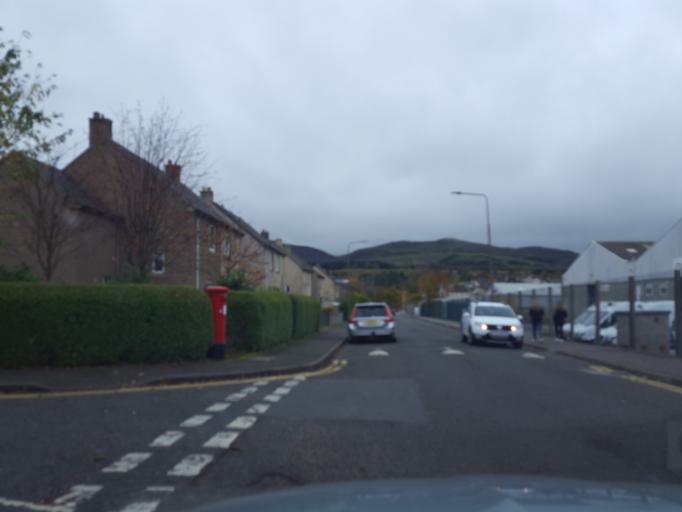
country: GB
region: Scotland
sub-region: Midlothian
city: Penicuik
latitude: 55.8331
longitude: -3.2167
